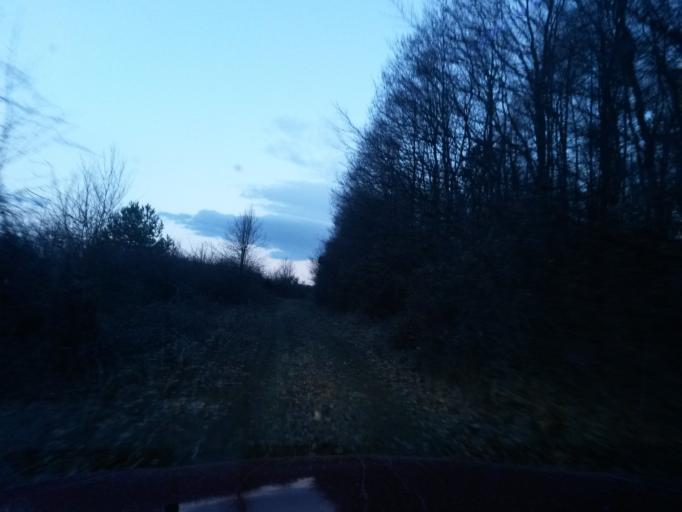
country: SK
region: Kosicky
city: Kosice
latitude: 48.6974
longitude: 21.3819
